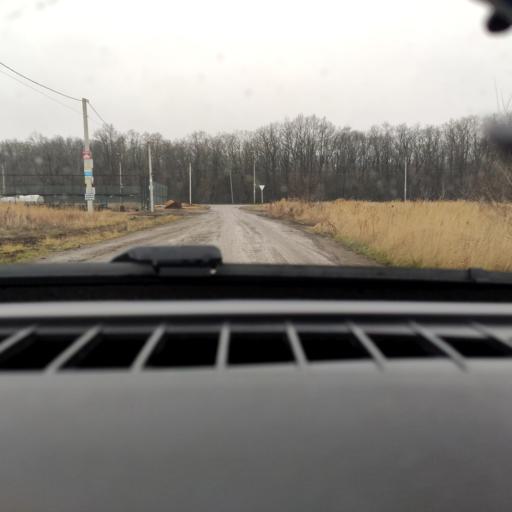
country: RU
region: Voronezj
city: Semiluki
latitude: 51.6592
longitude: 39.0403
